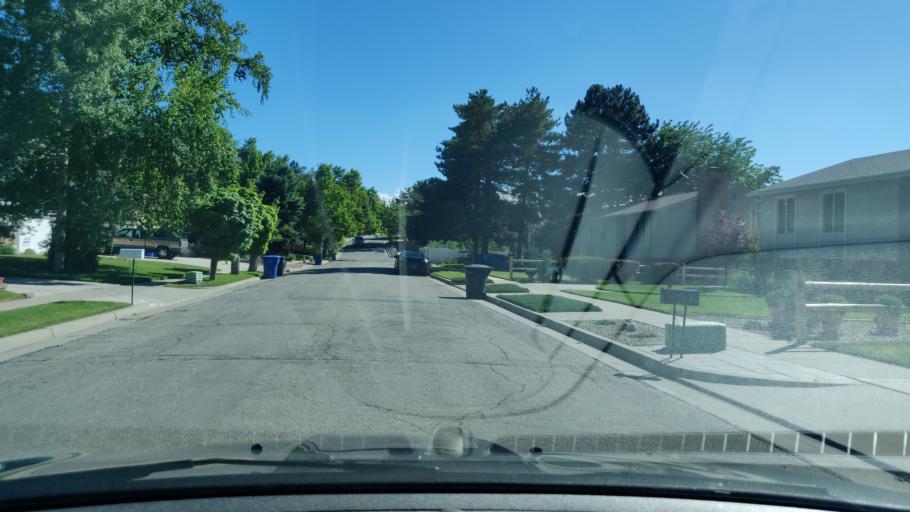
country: US
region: Utah
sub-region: Salt Lake County
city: Cottonwood Heights
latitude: 40.6155
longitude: -111.8079
